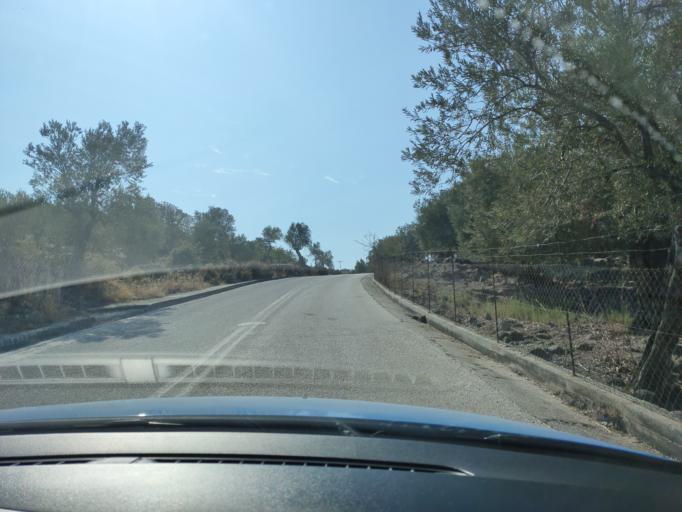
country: GR
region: North Aegean
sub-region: Nomos Lesvou
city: Mantamados
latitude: 39.3724
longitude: 26.3071
